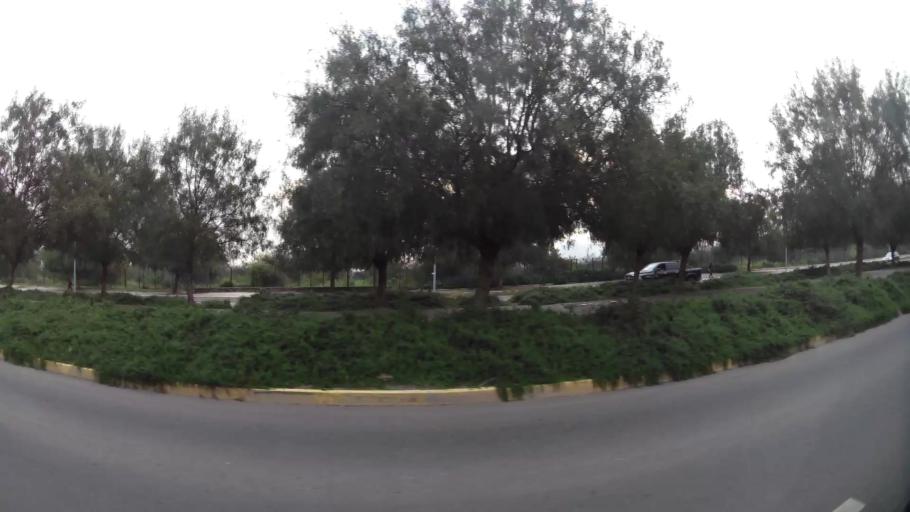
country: CL
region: Santiago Metropolitan
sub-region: Provincia de Chacabuco
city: Chicureo Abajo
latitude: -33.2683
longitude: -70.6235
